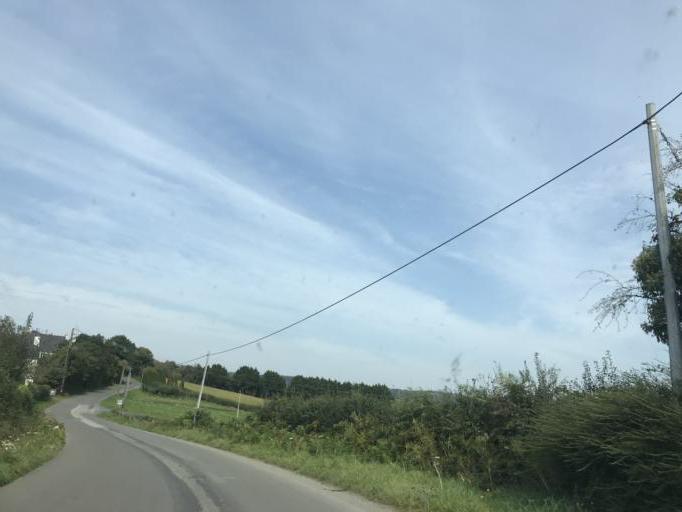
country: FR
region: Brittany
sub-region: Departement du Finistere
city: Brasparts
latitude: 48.3141
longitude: -3.9325
